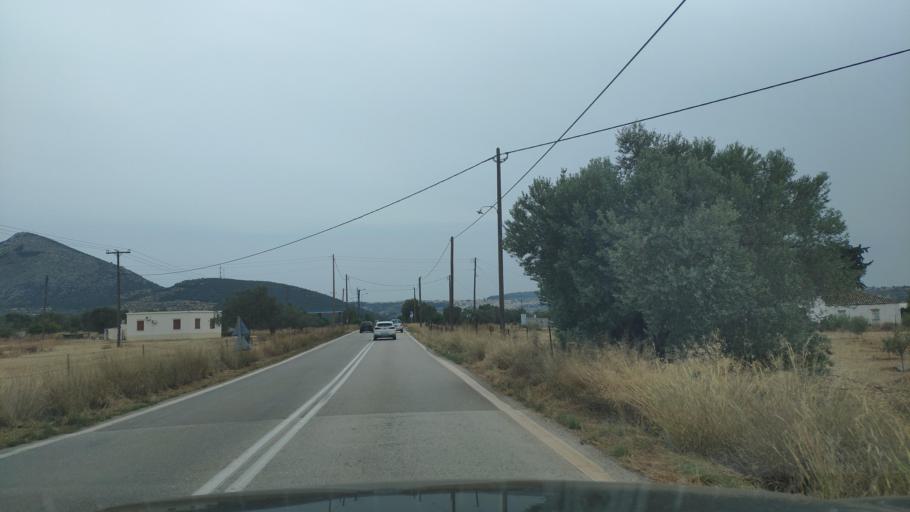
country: GR
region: Peloponnese
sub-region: Nomos Argolidos
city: Koilas
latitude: 37.4130
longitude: 23.1525
